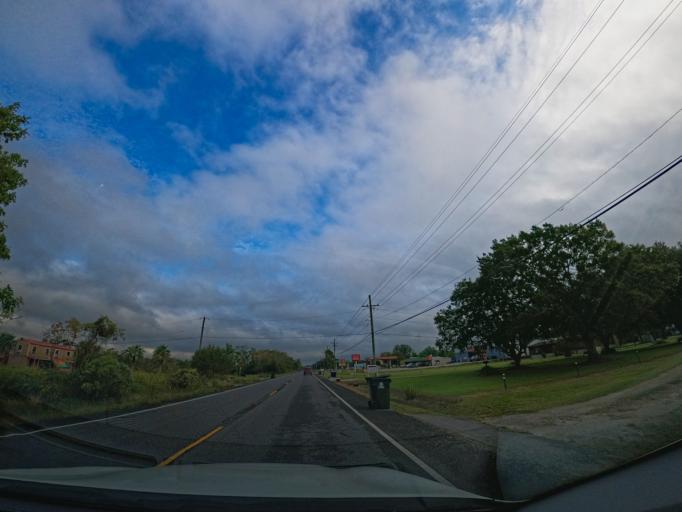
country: US
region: Louisiana
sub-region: Terrebonne Parish
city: Dulac
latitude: 29.4637
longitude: -90.7025
